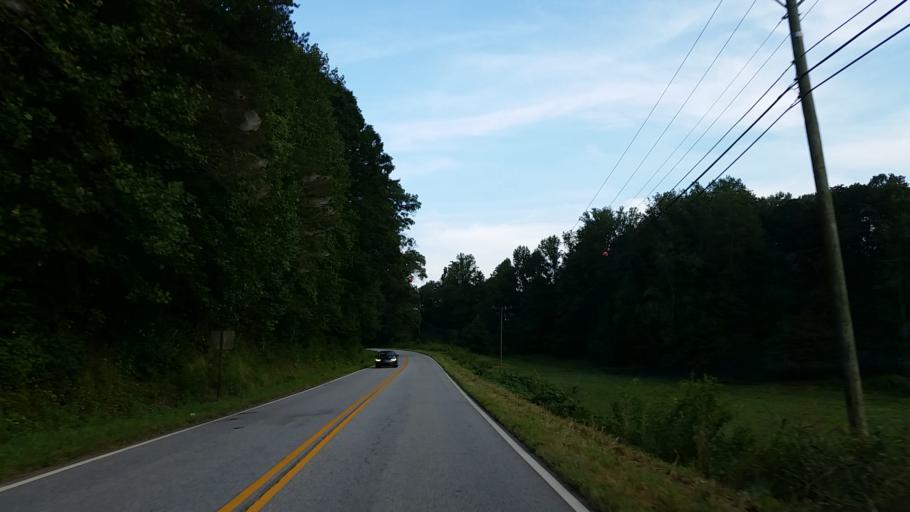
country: US
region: Georgia
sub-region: Lumpkin County
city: Dahlonega
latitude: 34.5752
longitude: -84.0162
